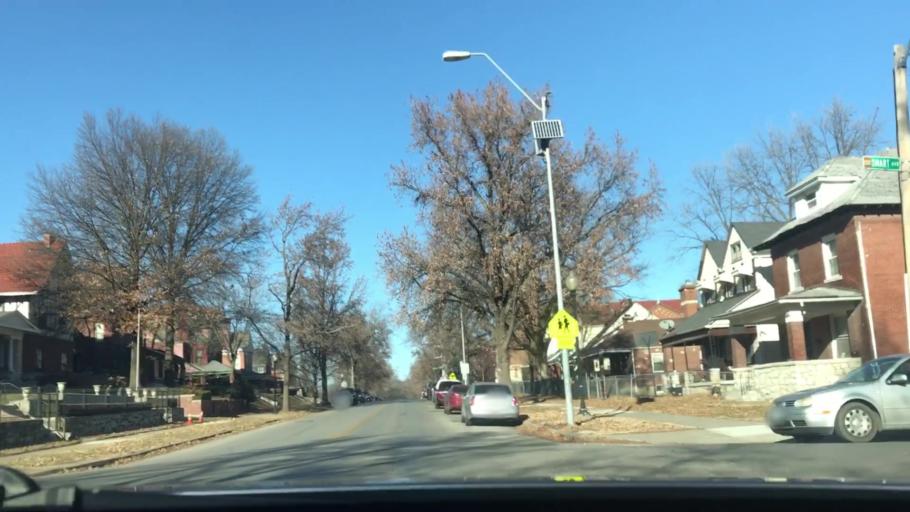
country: US
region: Missouri
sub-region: Clay County
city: North Kansas City
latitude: 39.1097
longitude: -94.5444
